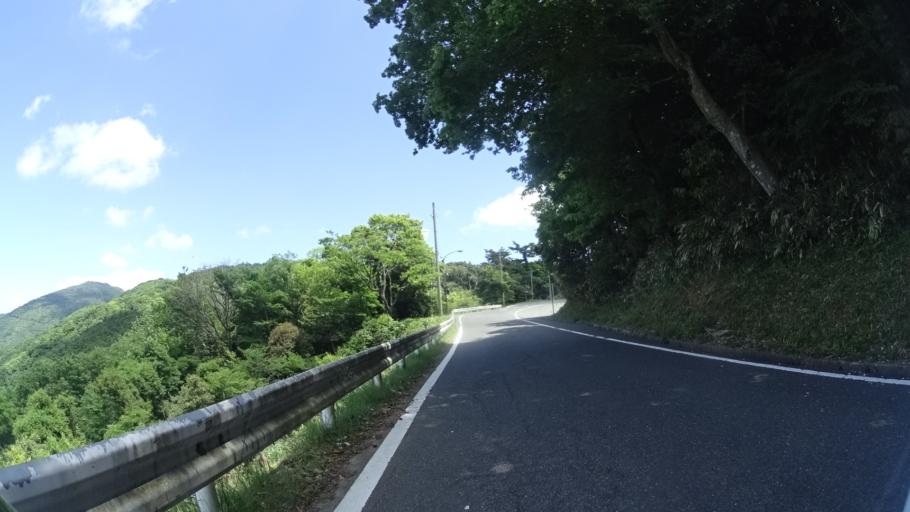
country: JP
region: Kyoto
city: Miyazu
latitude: 35.4791
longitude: 135.1604
